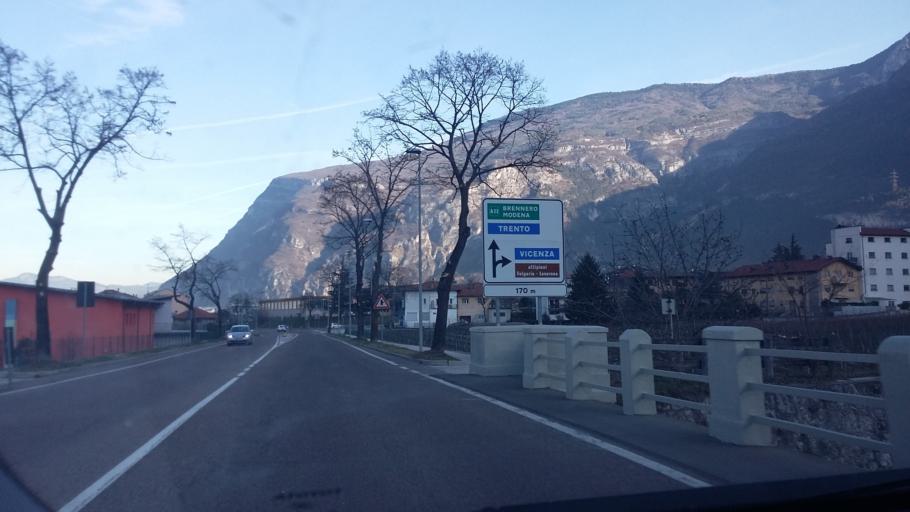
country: IT
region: Trentino-Alto Adige
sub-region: Provincia di Trento
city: Calliano
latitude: 45.9318
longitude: 11.0945
